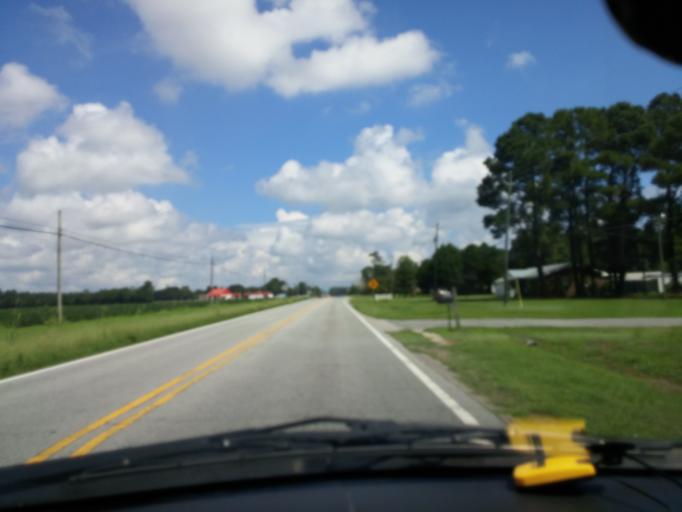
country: US
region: North Carolina
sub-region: Duplin County
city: Beulaville
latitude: 35.0698
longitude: -77.7368
